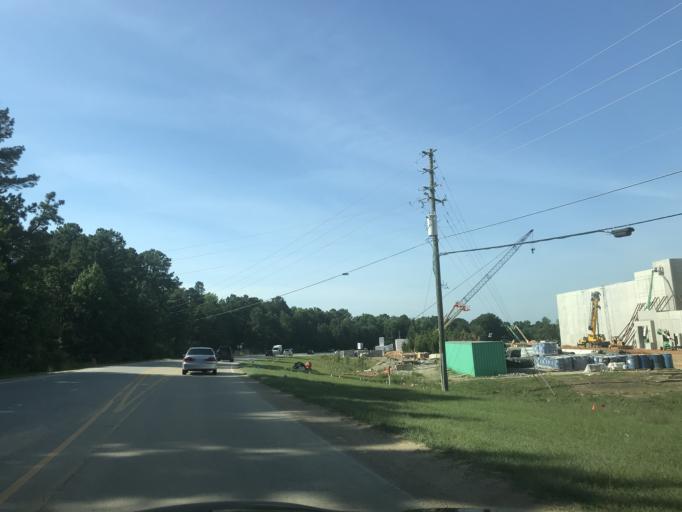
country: US
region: North Carolina
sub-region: Wake County
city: Garner
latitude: 35.7157
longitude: -78.5896
